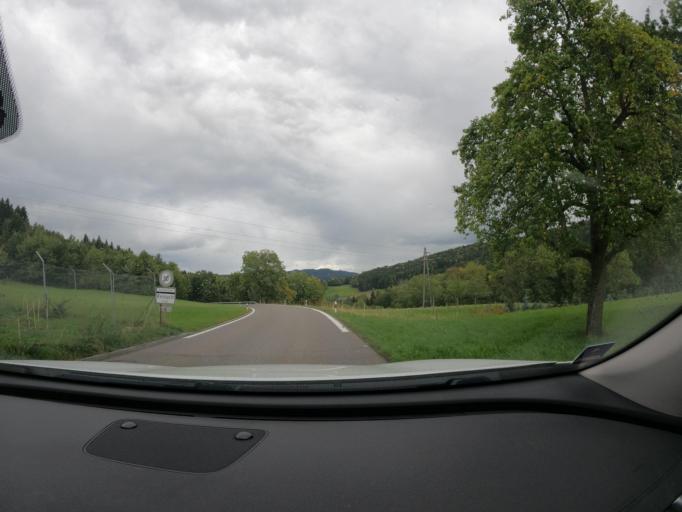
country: CH
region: Aargau
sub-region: Bezirk Kulm
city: Gontenschwil
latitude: 47.2486
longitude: 8.1308
